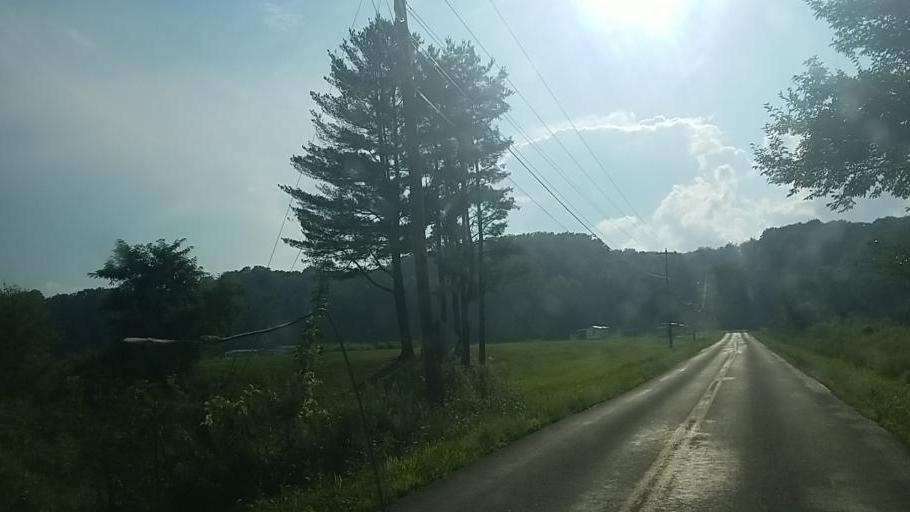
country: US
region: Ohio
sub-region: Wayne County
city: Wooster
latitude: 40.8580
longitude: -82.0078
